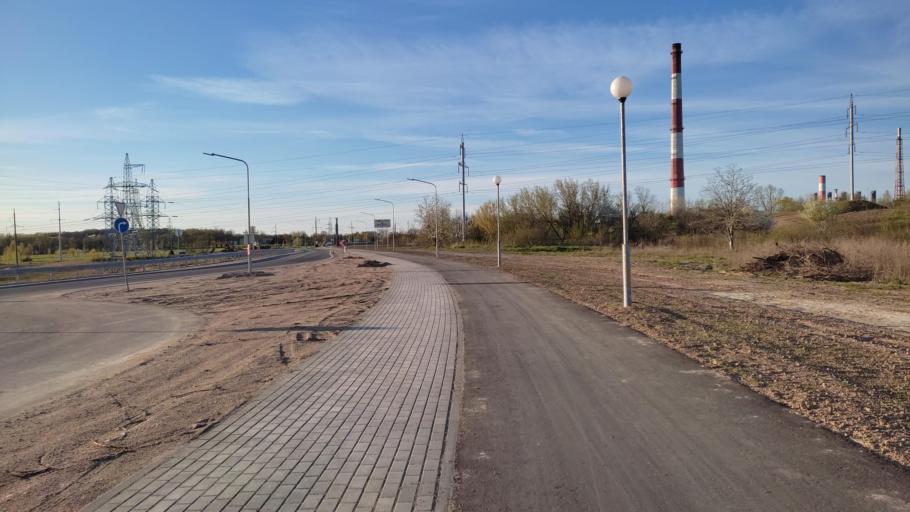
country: BY
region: Grodnenskaya
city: Hrodna
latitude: 53.6663
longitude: 23.8917
